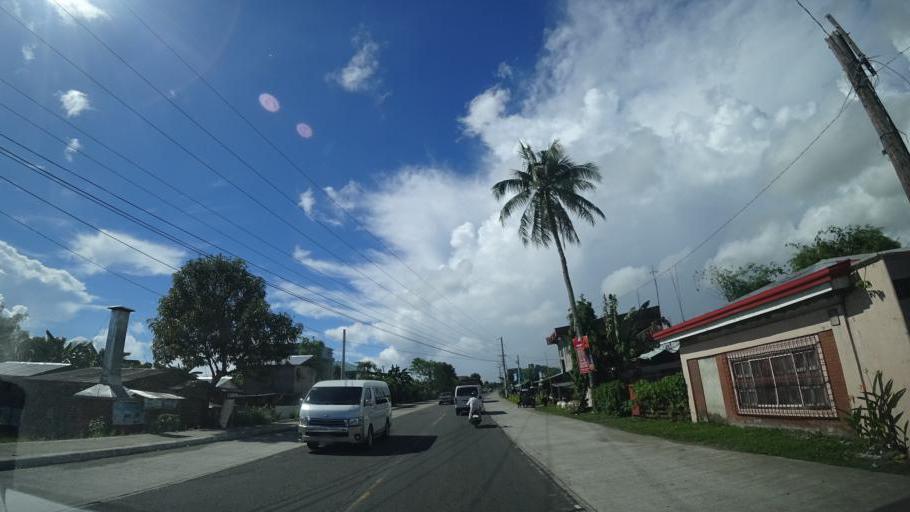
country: PH
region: Eastern Visayas
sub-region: Province of Leyte
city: Palo
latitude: 11.1408
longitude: 125.0050
